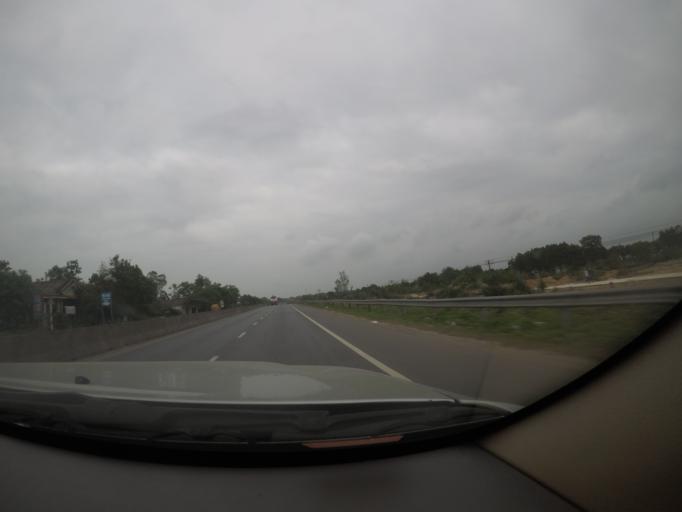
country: VN
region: Quang Tri
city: Hai Lang
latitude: 16.6644
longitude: 107.2731
